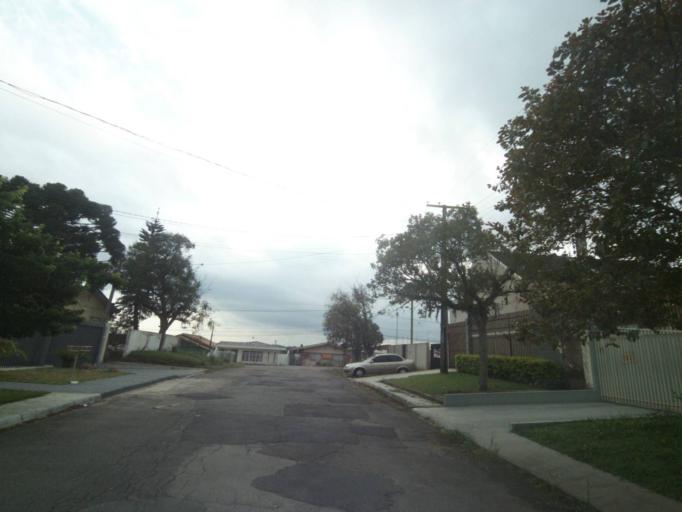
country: BR
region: Parana
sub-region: Pinhais
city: Pinhais
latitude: -25.4148
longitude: -49.2151
